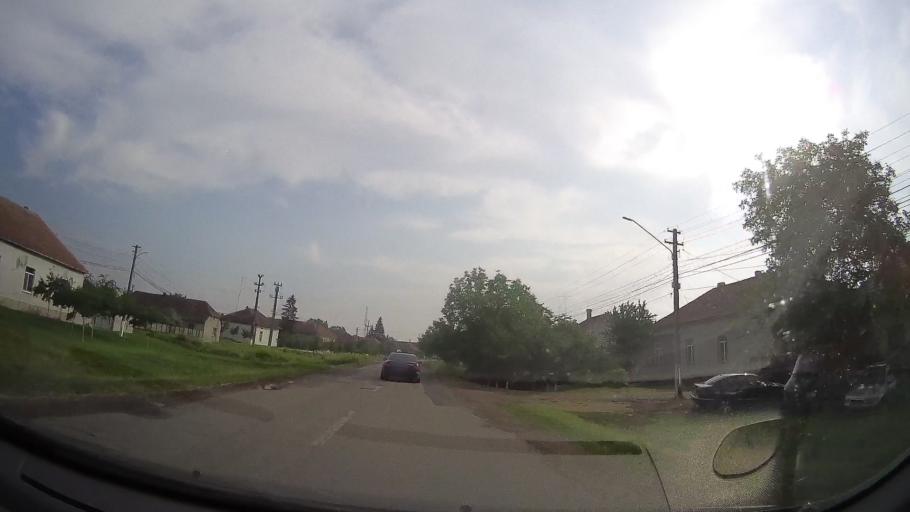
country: RO
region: Timis
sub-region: Comuna Peciu Nou
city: Peciu Nou
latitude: 45.5986
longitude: 21.0494
